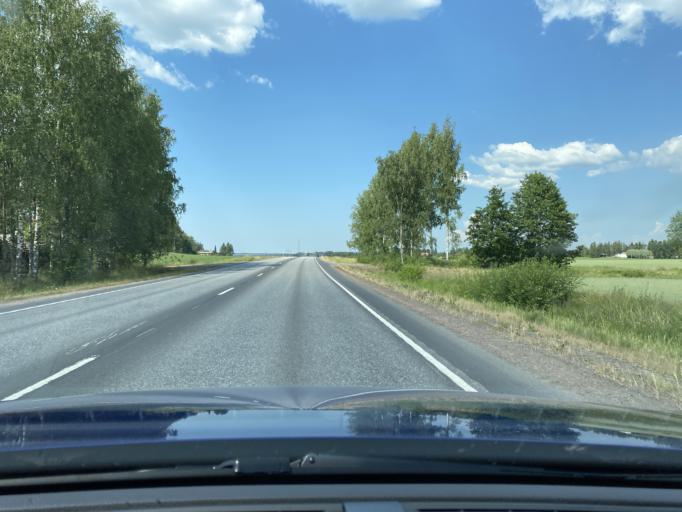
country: FI
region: Satakunta
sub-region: Rauma
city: Eura
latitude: 61.1486
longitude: 22.1014
